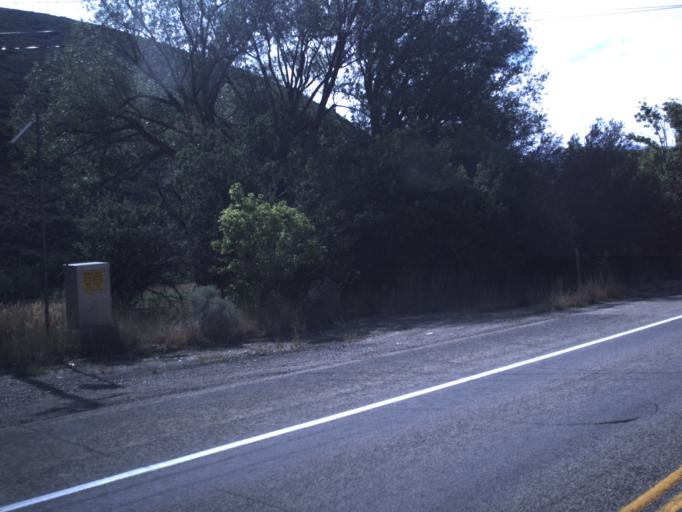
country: US
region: Utah
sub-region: Wasatch County
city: Heber
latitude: 40.4511
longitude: -111.3706
